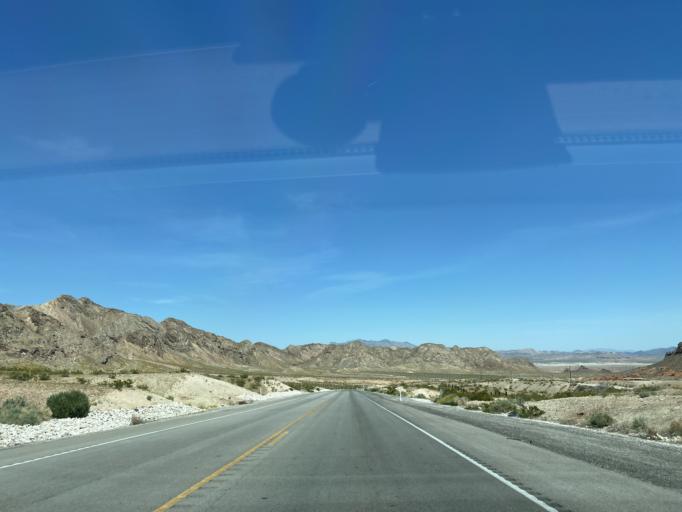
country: US
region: Nevada
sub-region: Clark County
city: Nellis Air Force Base
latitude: 36.2039
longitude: -114.9705
